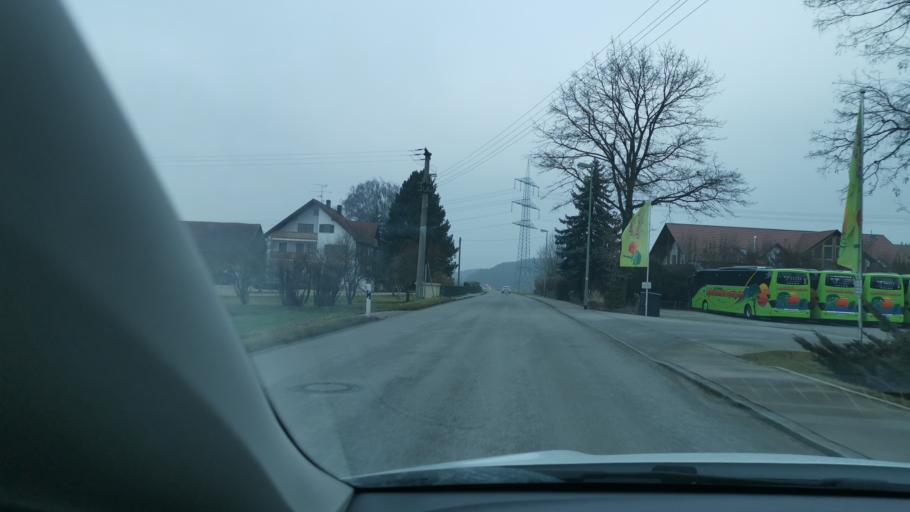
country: DE
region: Bavaria
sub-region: Swabia
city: Rehling
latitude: 48.4982
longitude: 10.9209
